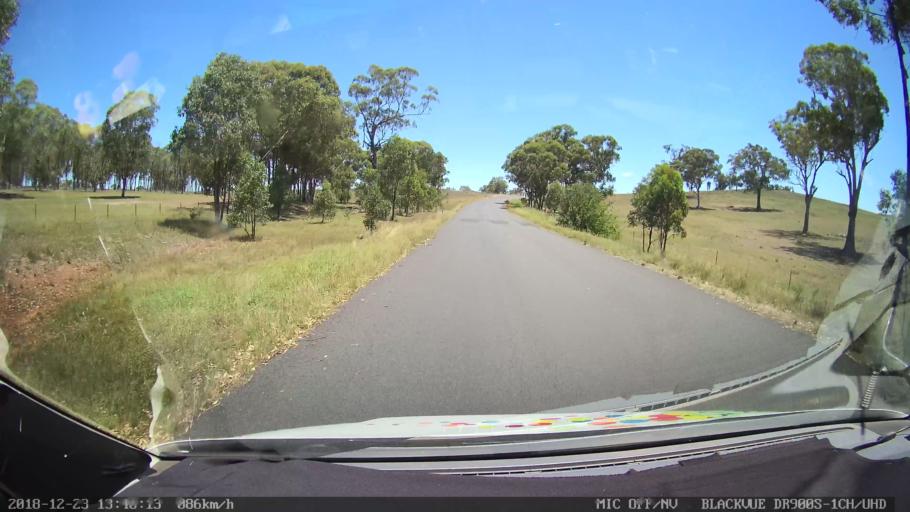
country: AU
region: New South Wales
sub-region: Armidale Dumaresq
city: Armidale
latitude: -30.4649
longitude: 151.1934
